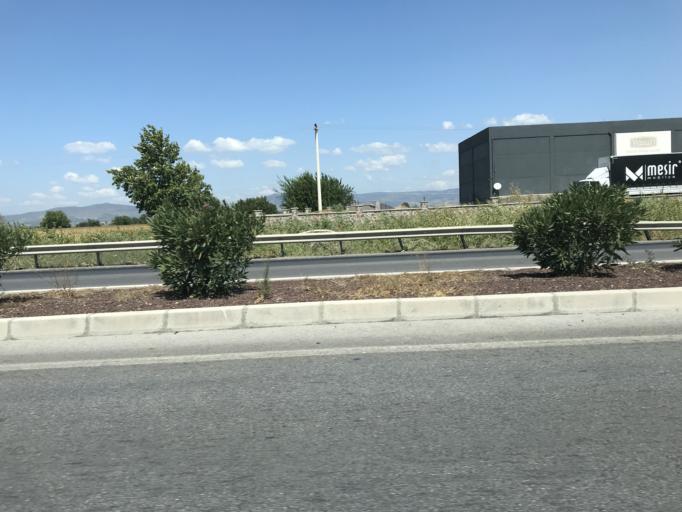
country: TR
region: Manisa
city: Saruhanli
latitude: 38.6918
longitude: 27.5043
